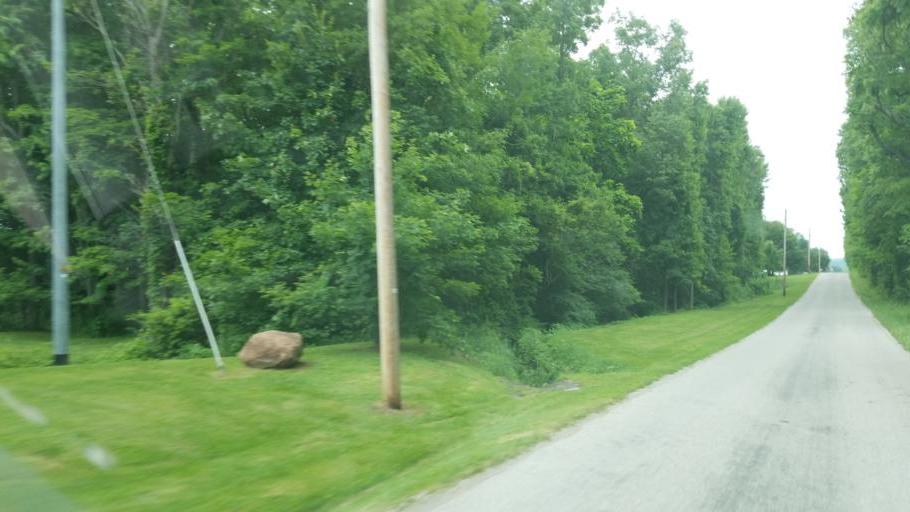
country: US
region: Ohio
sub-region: Sandusky County
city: Bellville
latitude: 40.6009
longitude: -82.5679
